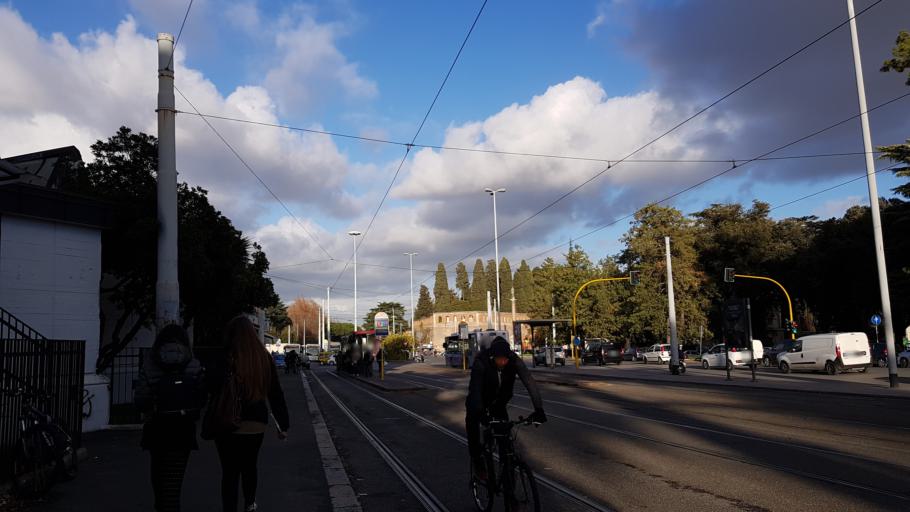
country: IT
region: Latium
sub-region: Citta metropolitana di Roma Capitale
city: Rome
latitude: 41.9012
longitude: 12.5181
